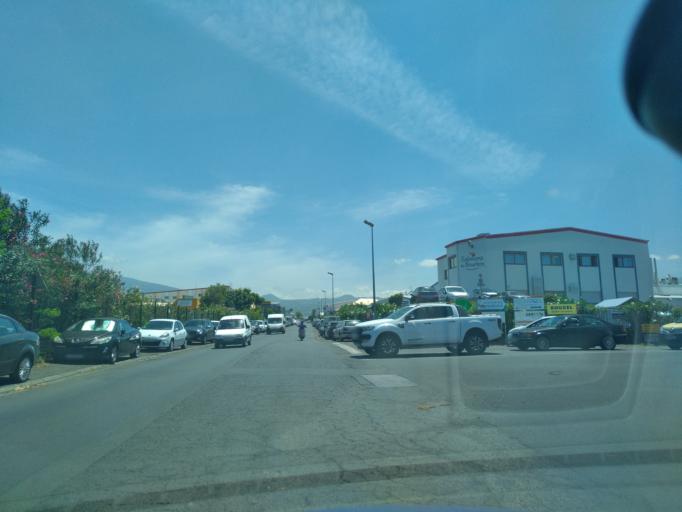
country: RE
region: Reunion
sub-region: Reunion
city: Saint-Pierre
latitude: -21.3190
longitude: 55.4517
